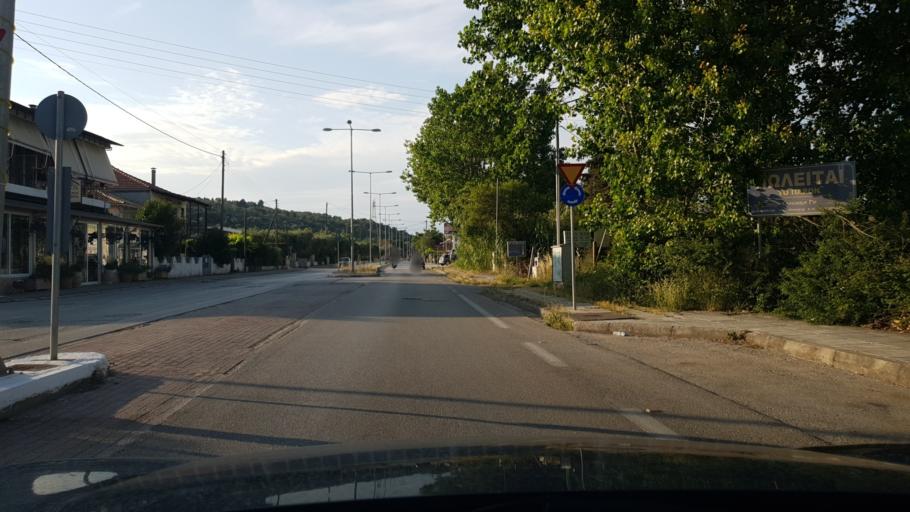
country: GR
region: Ionian Islands
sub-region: Lefkada
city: Lefkada
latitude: 38.7999
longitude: 20.7161
